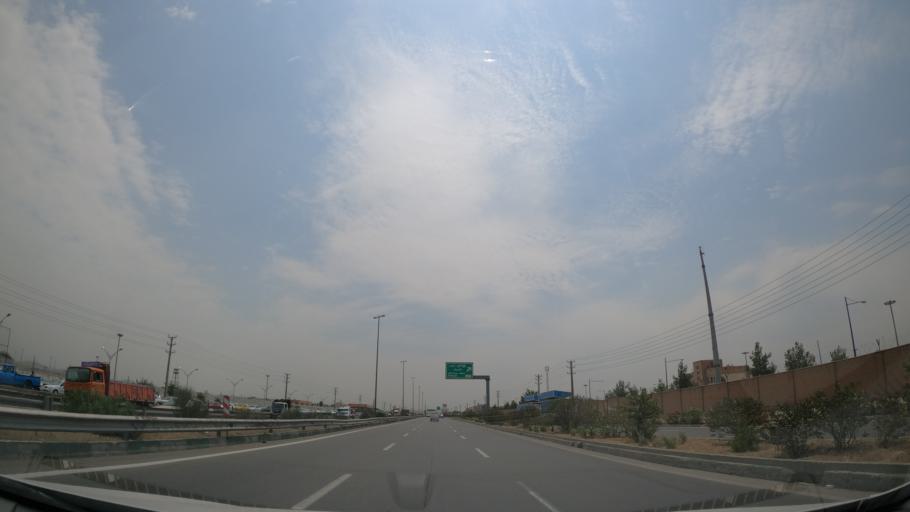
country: IR
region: Tehran
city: Shahr-e Qods
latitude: 35.6992
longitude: 51.1938
